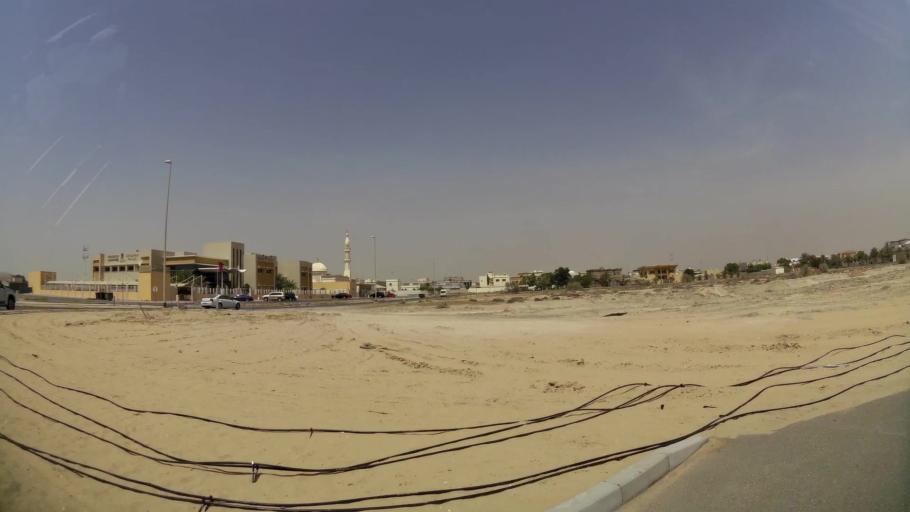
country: AE
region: Ash Shariqah
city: Sharjah
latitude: 25.2415
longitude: 55.4192
